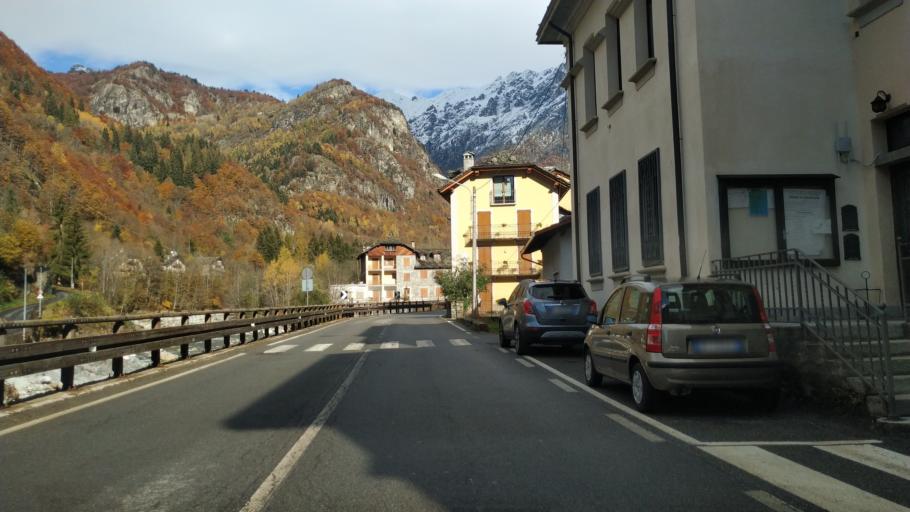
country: IT
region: Piedmont
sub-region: Provincia di Vercelli
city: Campertogno
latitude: 45.7992
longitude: 8.0319
